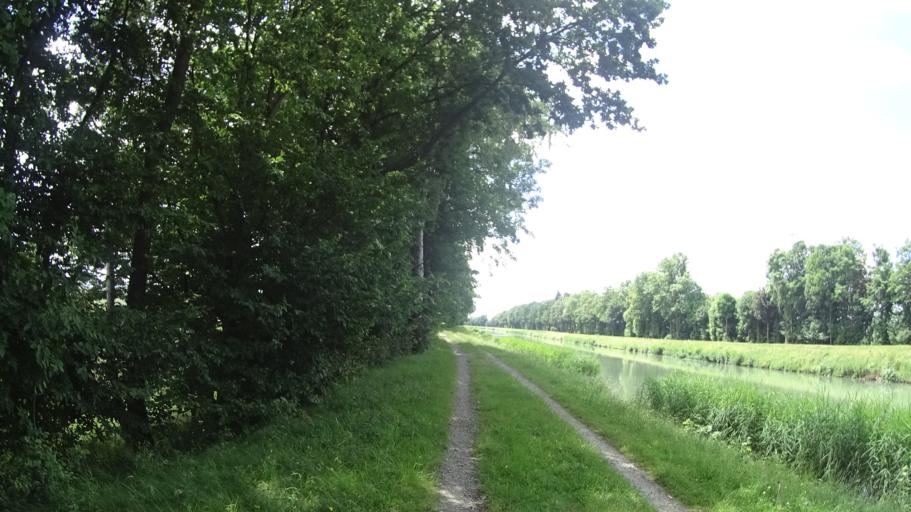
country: DE
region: Lower Saxony
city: Algermissen
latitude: 52.2383
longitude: 9.9460
